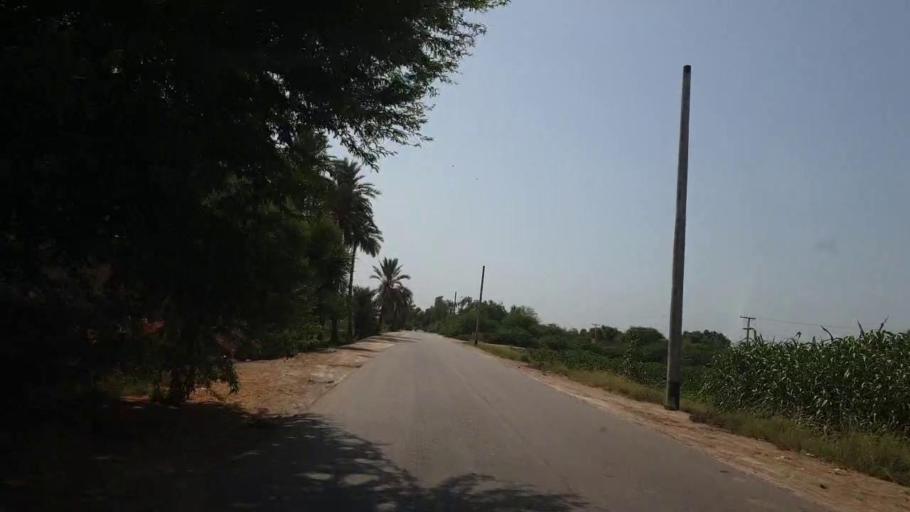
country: PK
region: Sindh
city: Bozdar
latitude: 27.1210
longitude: 68.5484
